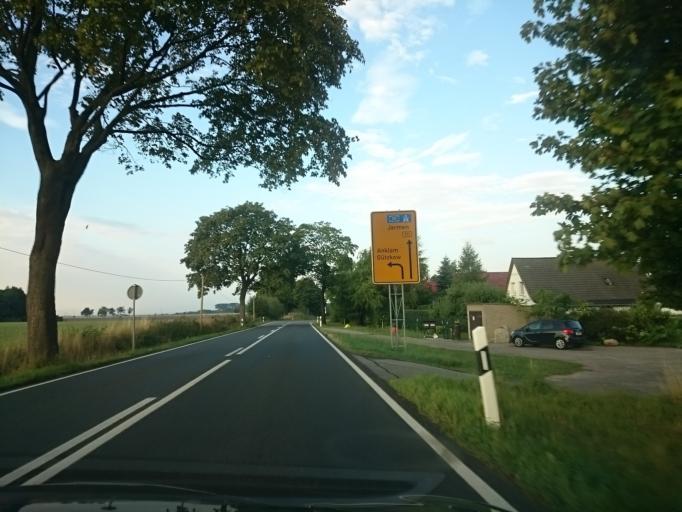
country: DE
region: Mecklenburg-Vorpommern
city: Gross Kiesow
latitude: 53.9371
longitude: 13.4483
